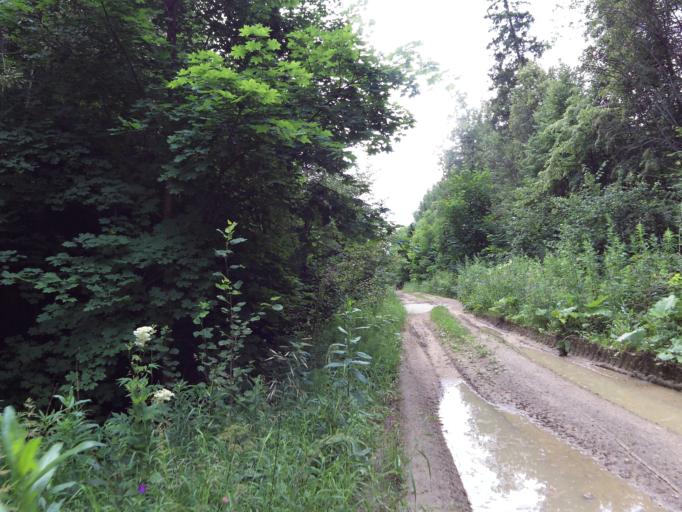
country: RU
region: Moskovskaya
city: Popovo
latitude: 54.9886
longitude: 37.6920
